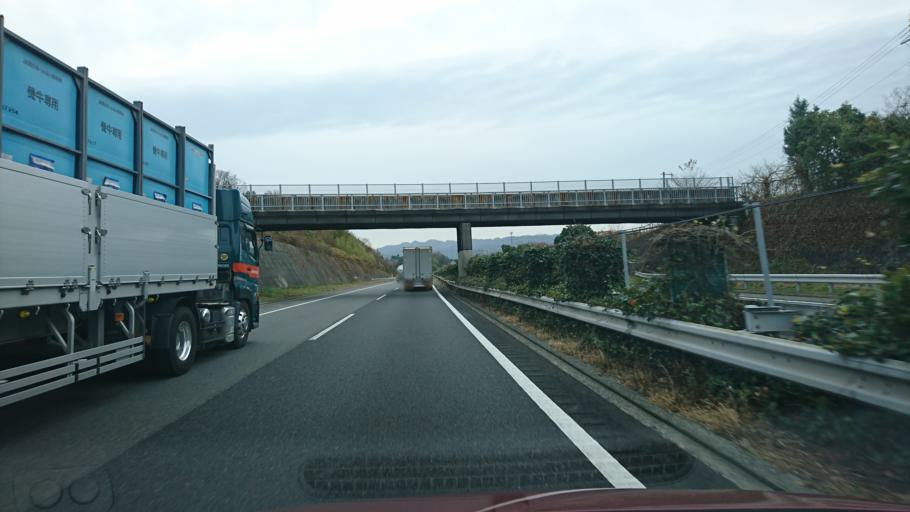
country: JP
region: Hyogo
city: Sandacho
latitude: 34.8297
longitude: 135.1688
